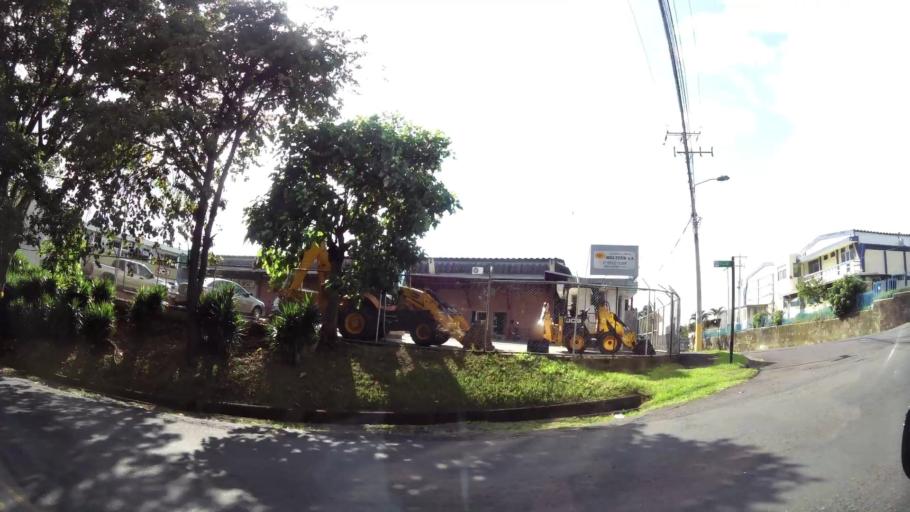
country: CR
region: San Jose
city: San Rafael
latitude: 9.9363
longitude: -84.1209
